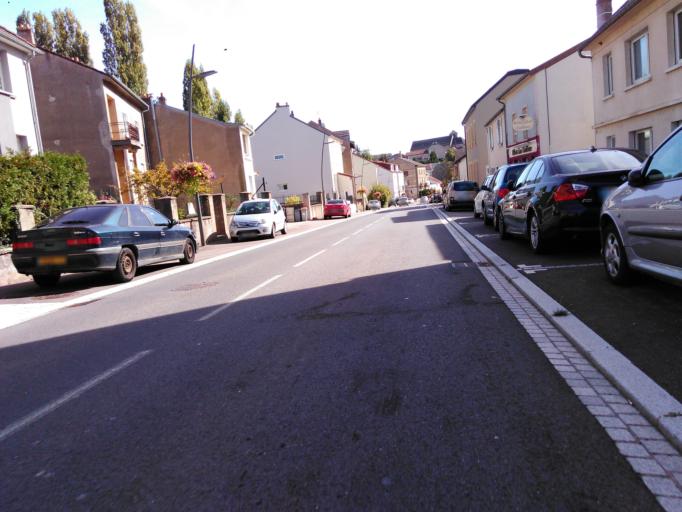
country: FR
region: Lorraine
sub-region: Departement de la Moselle
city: Hettange-Grande
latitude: 49.4094
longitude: 6.1479
